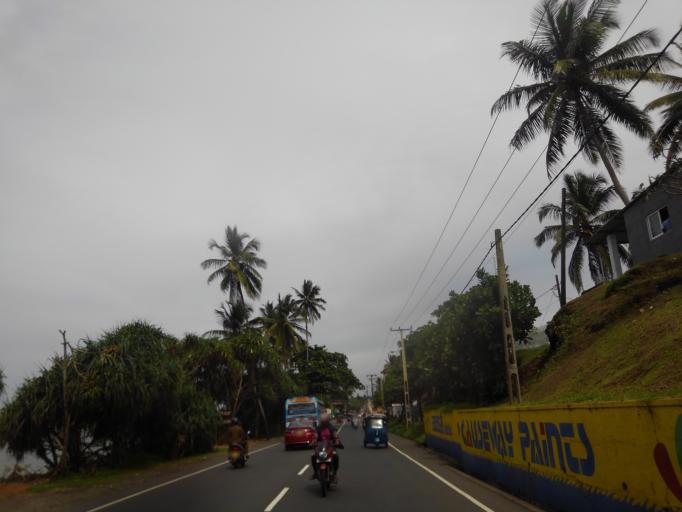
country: LK
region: Western
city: Beruwala
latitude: 6.4802
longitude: 79.9833
